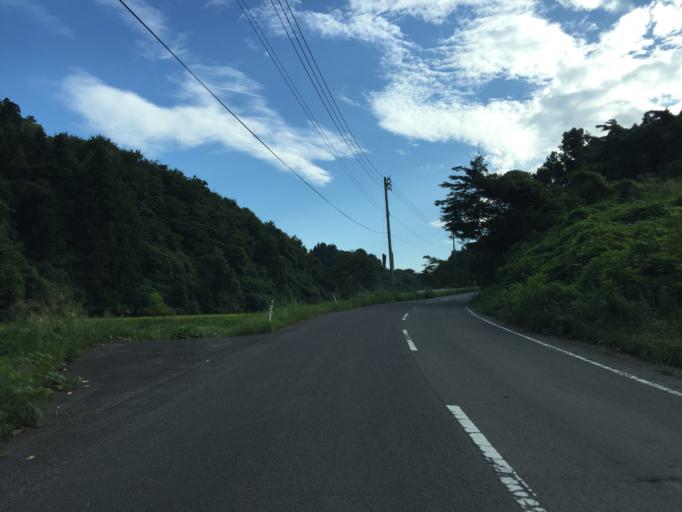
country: JP
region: Fukushima
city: Fukushima-shi
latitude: 37.6601
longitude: 140.5716
